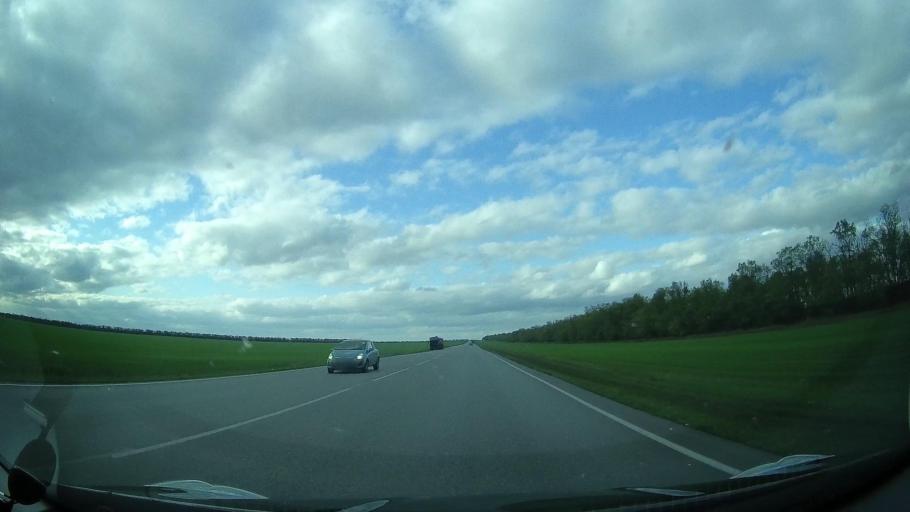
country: RU
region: Rostov
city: Kagal'nitskaya
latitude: 46.9041
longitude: 40.1199
